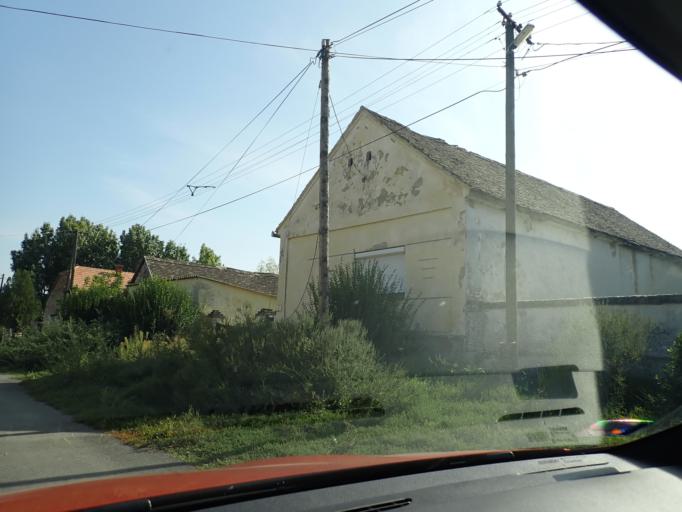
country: HU
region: Baranya
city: Boly
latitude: 45.9936
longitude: 18.5136
